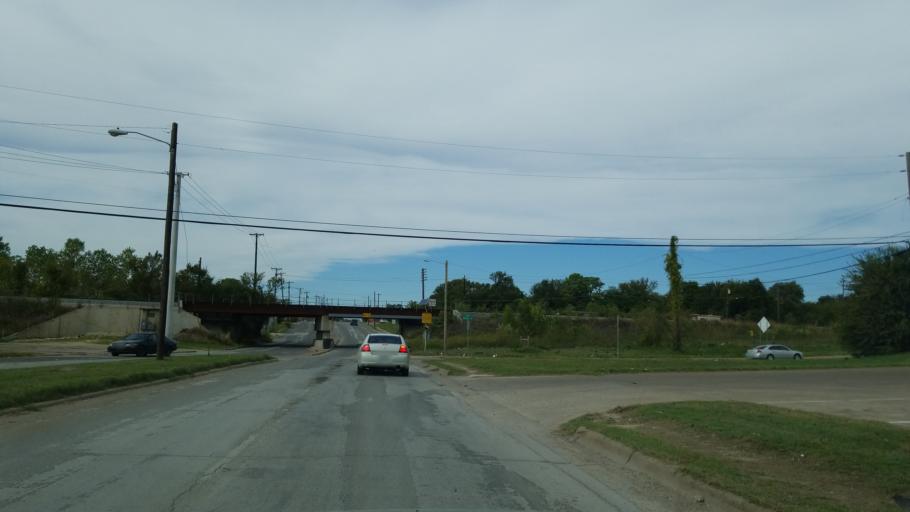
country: US
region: Texas
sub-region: Dallas County
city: Dallas
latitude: 32.7575
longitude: -96.7403
